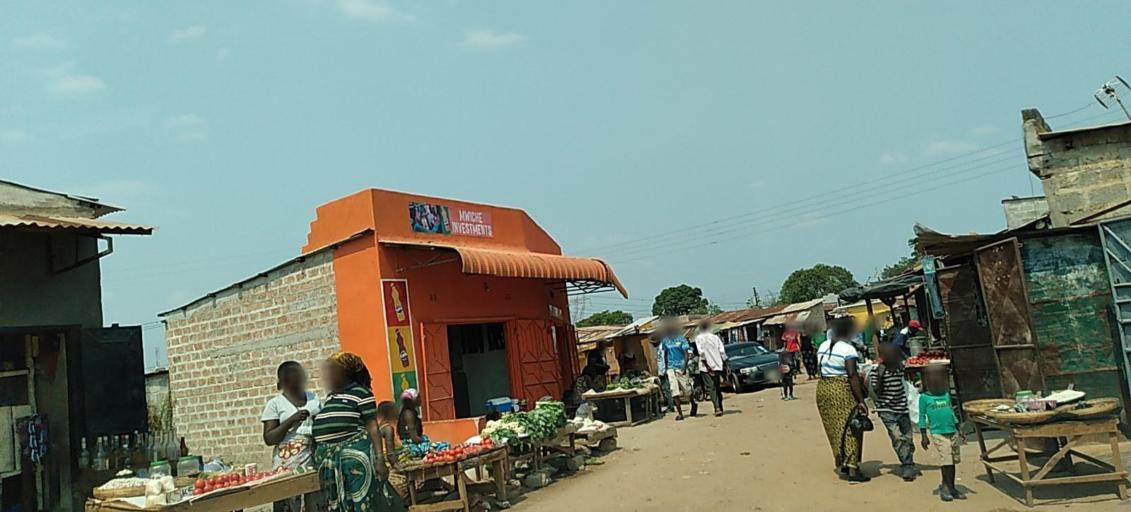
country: ZM
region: Copperbelt
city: Chambishi
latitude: -12.6318
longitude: 28.0707
